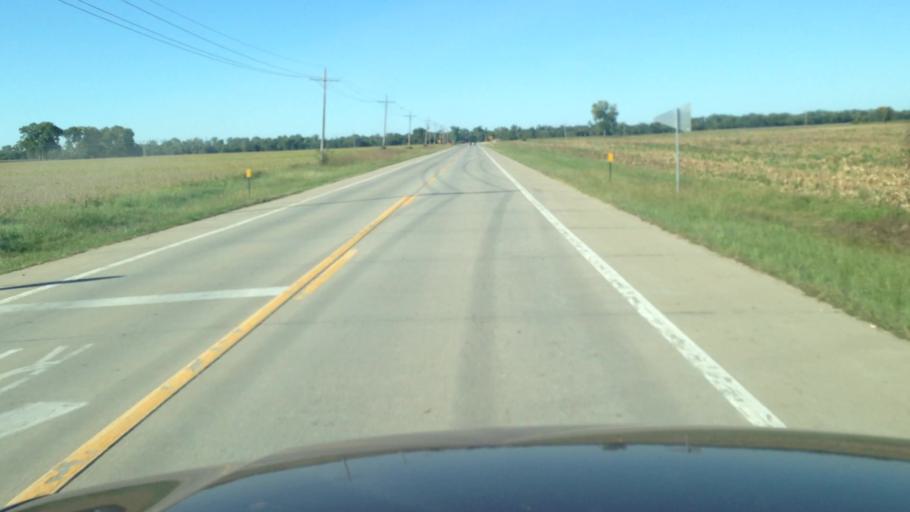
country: US
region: Kansas
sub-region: Douglas County
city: Lawrence
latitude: 38.9520
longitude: -95.1768
